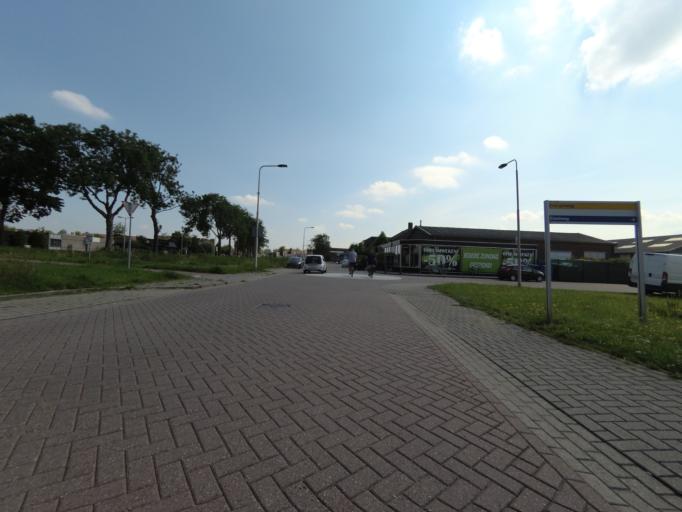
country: NL
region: Gelderland
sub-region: Gemeente Culemborg
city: Culemborg
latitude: 51.9442
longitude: 5.2160
